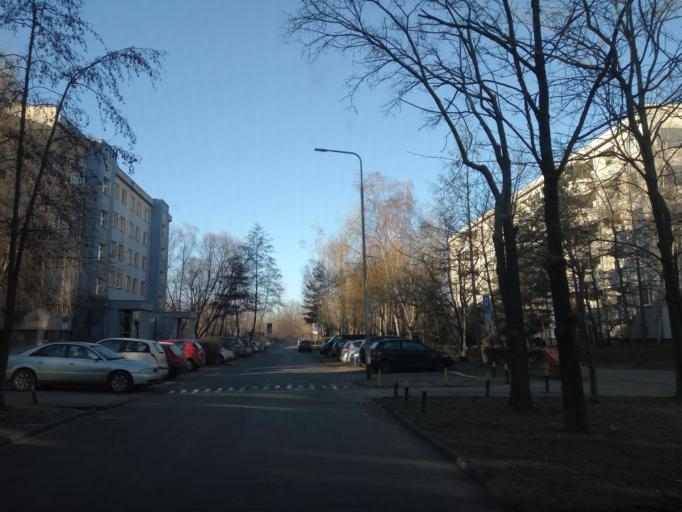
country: PL
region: Lower Silesian Voivodeship
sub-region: Powiat wroclawski
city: Wroclaw
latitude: 51.1267
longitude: 16.9578
